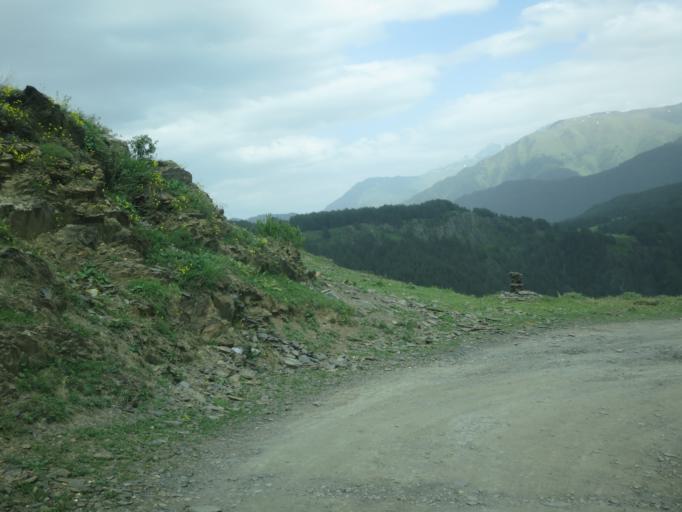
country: RU
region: Chechnya
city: Itum-Kali
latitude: 42.3744
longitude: 45.6336
